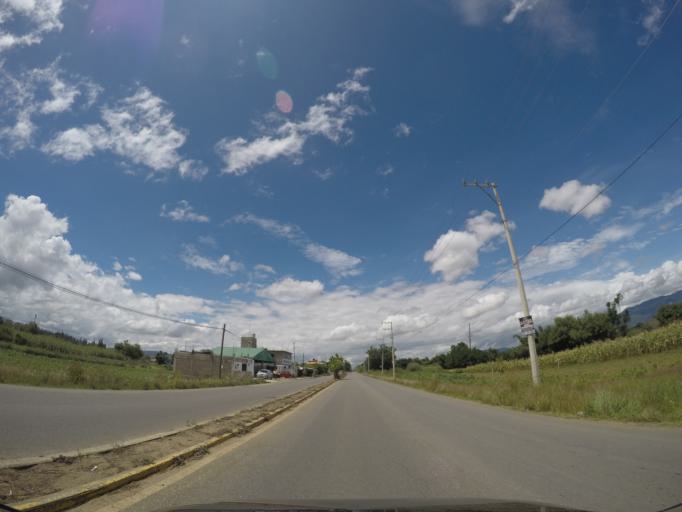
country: MX
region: Oaxaca
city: San Raymundo Jalpam
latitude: 16.9771
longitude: -96.7495
